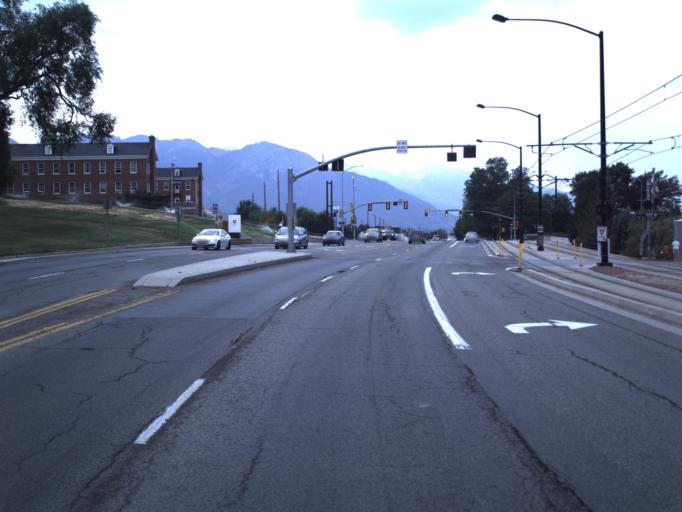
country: US
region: Utah
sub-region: Salt Lake County
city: Salt Lake City
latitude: 40.7638
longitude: -111.8362
